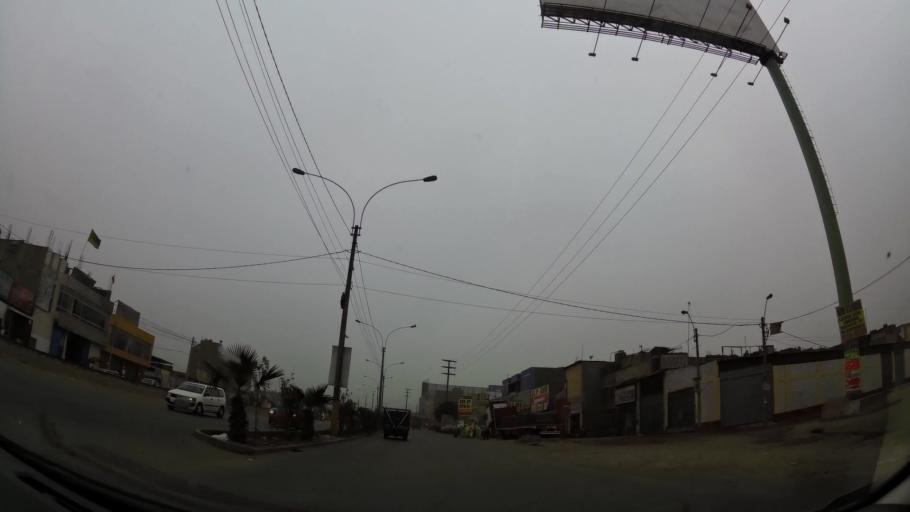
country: PE
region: Lima
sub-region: Lima
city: Santa Maria
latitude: -12.0054
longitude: -76.8462
